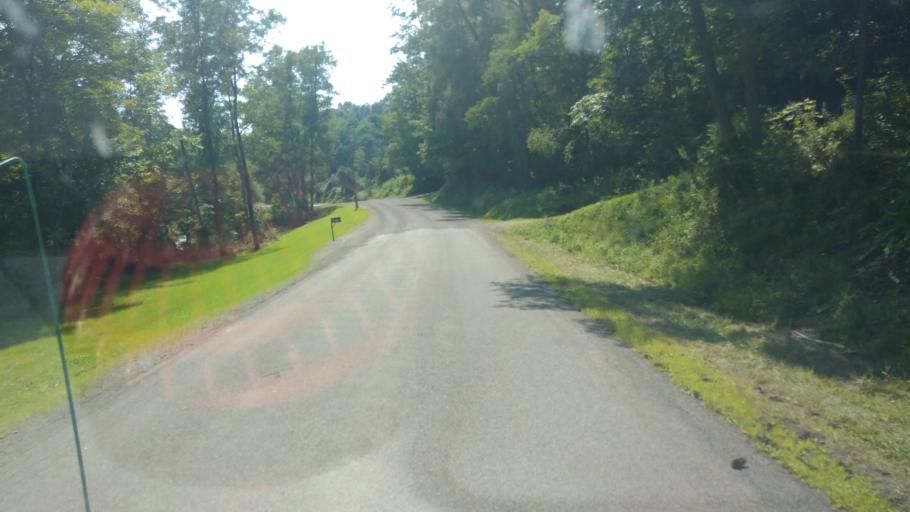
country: US
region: New York
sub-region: Steuben County
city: Canisteo
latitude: 42.3075
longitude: -77.6074
